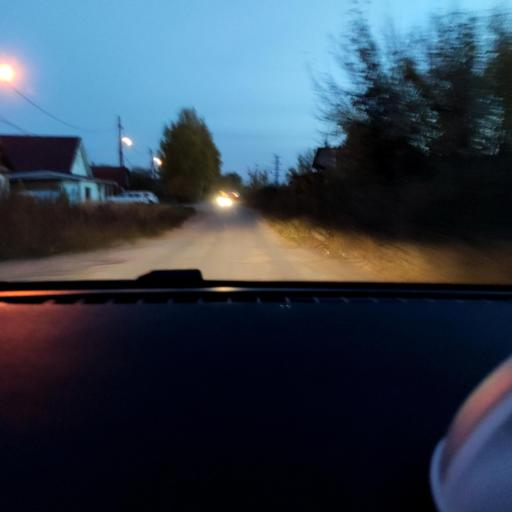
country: RU
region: Samara
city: Petra-Dubrava
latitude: 53.2979
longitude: 50.3039
